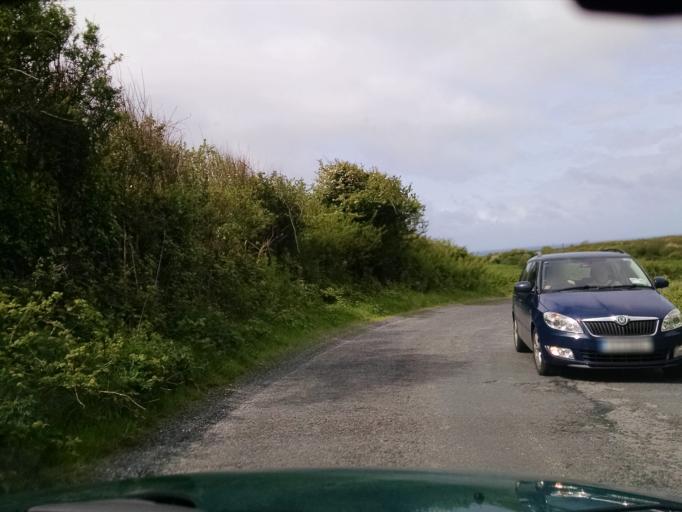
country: IE
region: Connaught
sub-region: County Galway
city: Bearna
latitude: 53.0514
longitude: -9.3445
